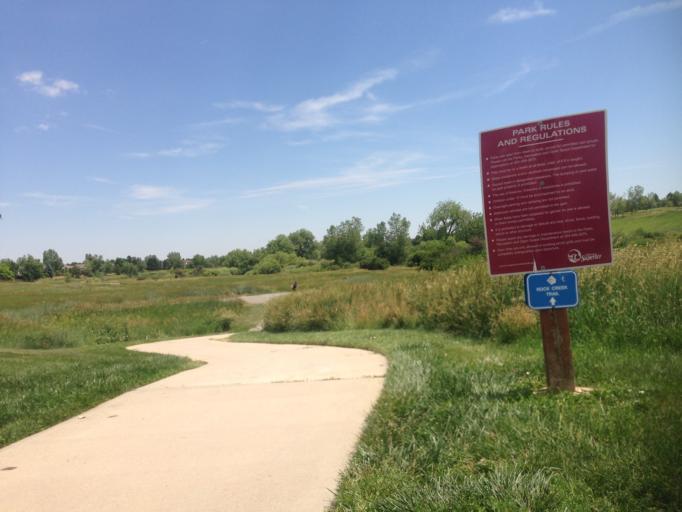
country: US
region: Colorado
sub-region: Boulder County
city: Superior
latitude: 39.9303
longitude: -105.1591
